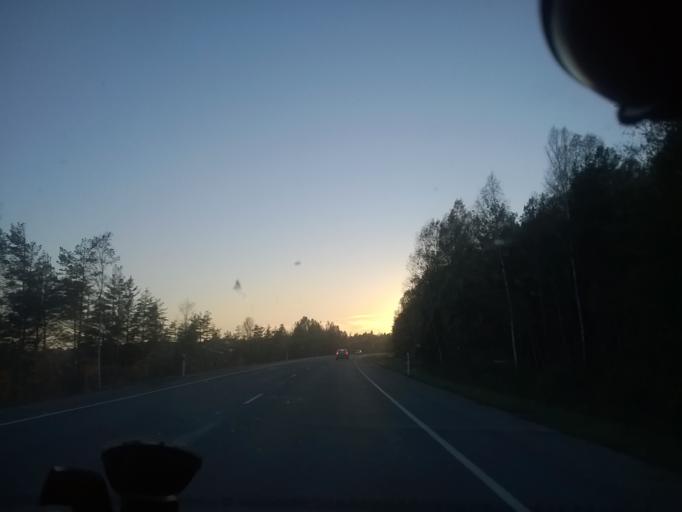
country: EE
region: Harju
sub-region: Nissi vald
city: Turba
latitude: 58.9951
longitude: 24.0678
